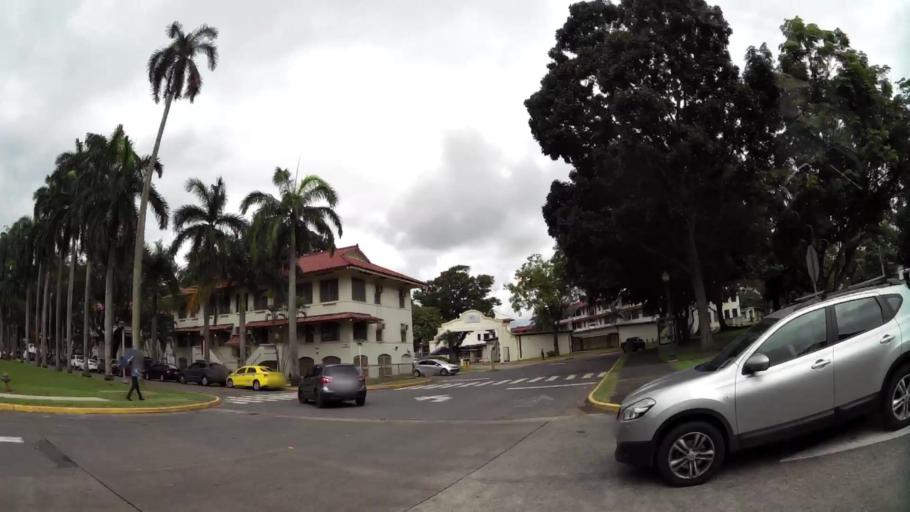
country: PA
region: Panama
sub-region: Distrito de Panama
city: Ancon
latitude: 8.9579
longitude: -79.5562
